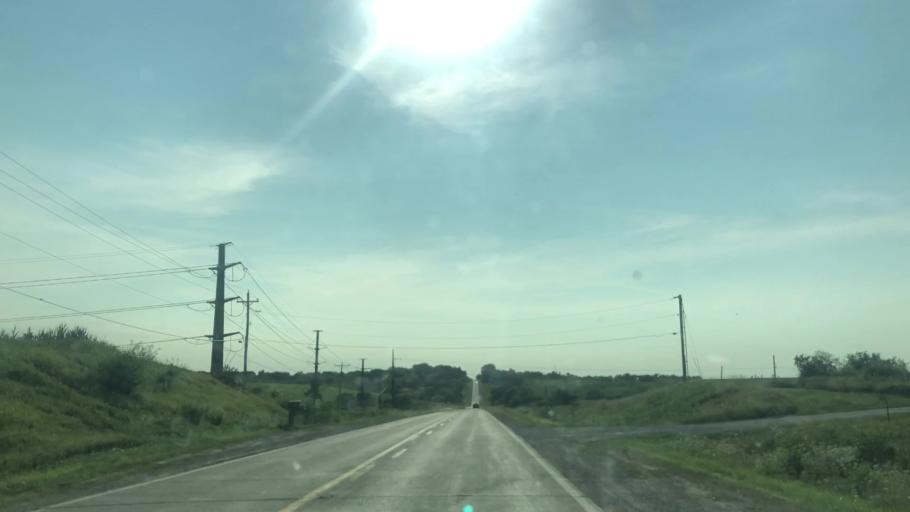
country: US
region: Iowa
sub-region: Marshall County
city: Marshalltown
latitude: 42.0490
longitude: -92.9625
